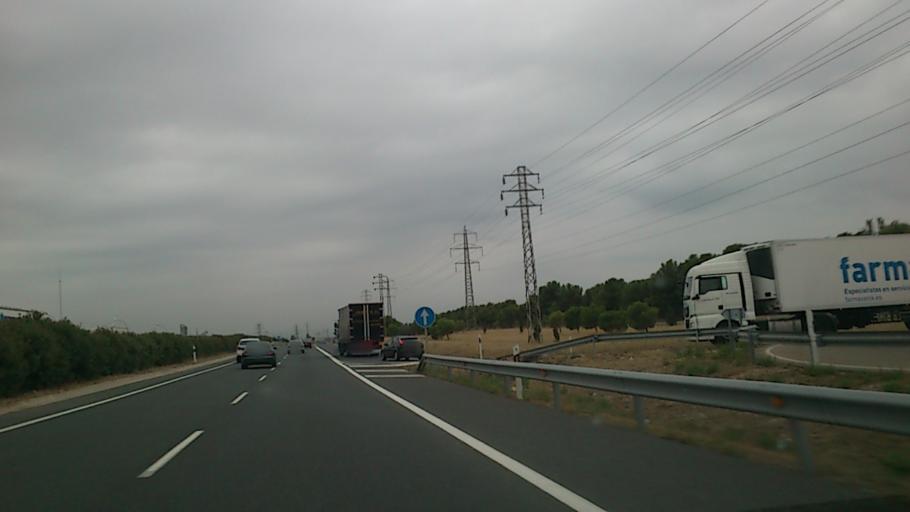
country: ES
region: Aragon
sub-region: Provincia de Zaragoza
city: Villanueva de Gallego
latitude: 41.7191
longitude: -0.8563
